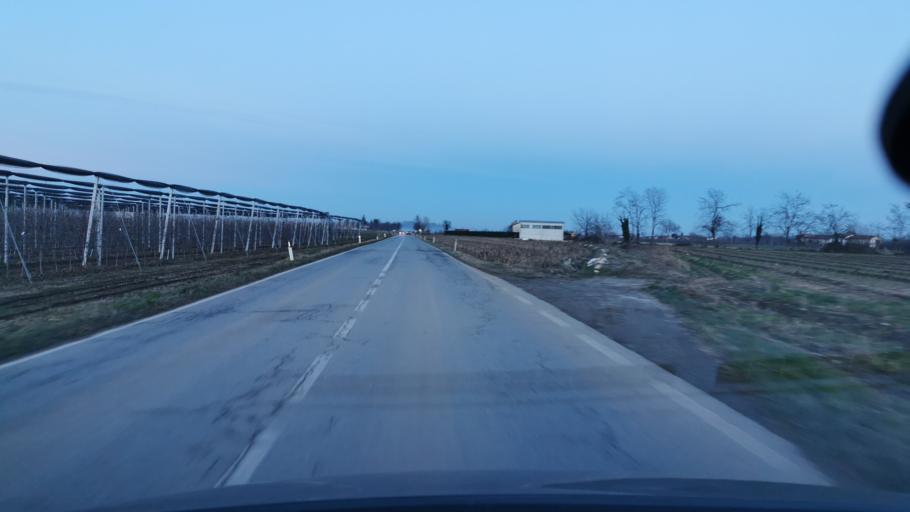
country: IT
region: Piedmont
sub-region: Provincia di Cuneo
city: Caraglio
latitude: 44.4301
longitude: 7.4388
